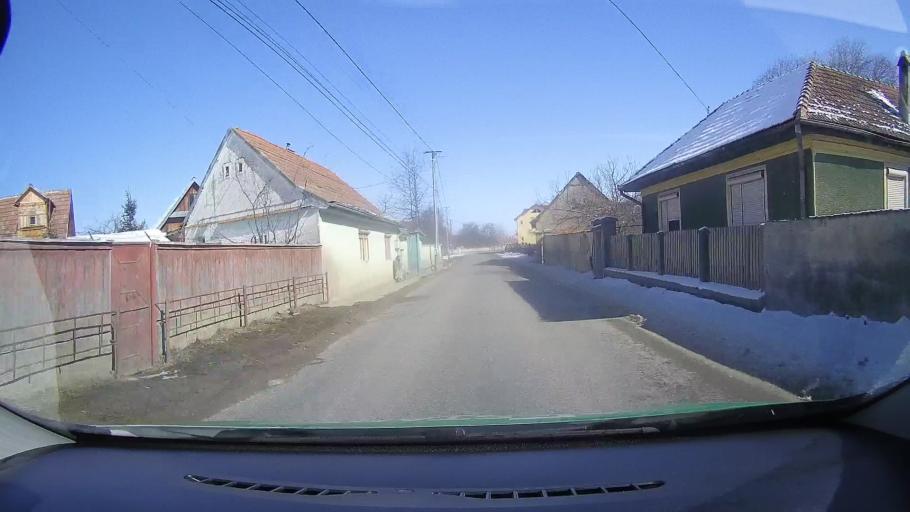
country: RO
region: Brasov
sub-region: Oras Victoria
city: Victoria
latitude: 45.7439
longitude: 24.7383
